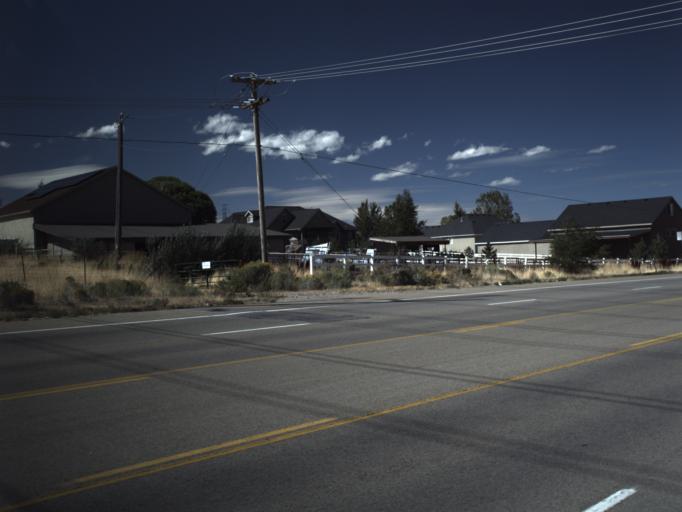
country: US
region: Utah
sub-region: Salt Lake County
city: Bluffdale
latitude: 40.4712
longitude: -111.9466
